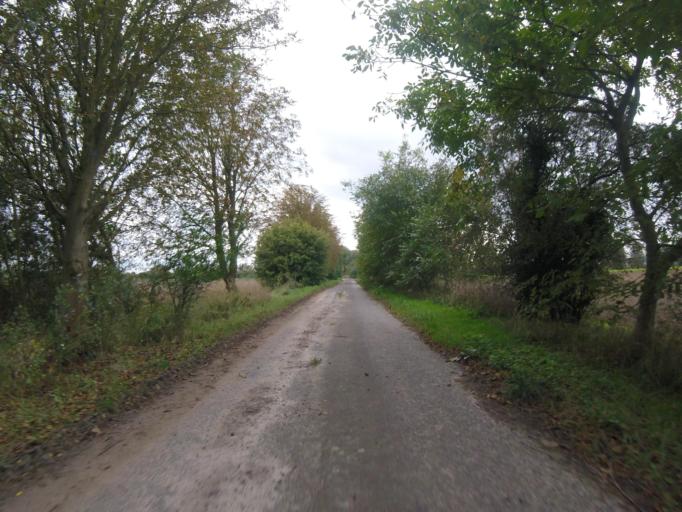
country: DE
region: Brandenburg
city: Mittenwalde
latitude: 52.2664
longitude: 13.5255
